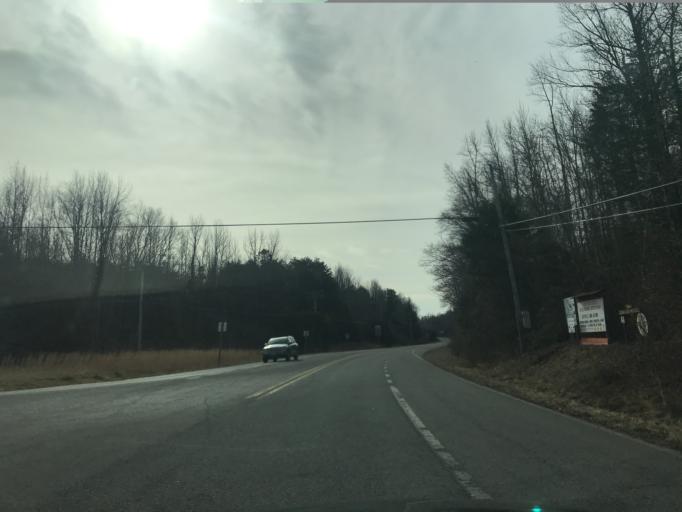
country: US
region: Virginia
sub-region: Prince William County
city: Quantico Station
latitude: 38.4407
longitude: -77.1991
